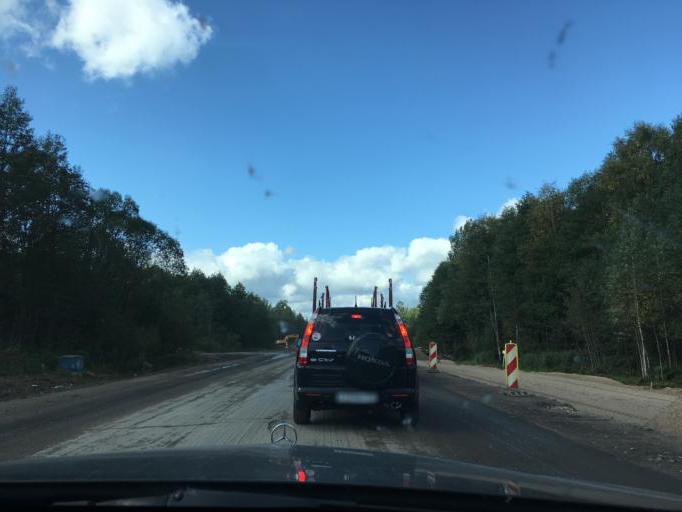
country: RU
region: Pskov
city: Novosokol'niki
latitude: 56.2728
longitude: 30.3459
